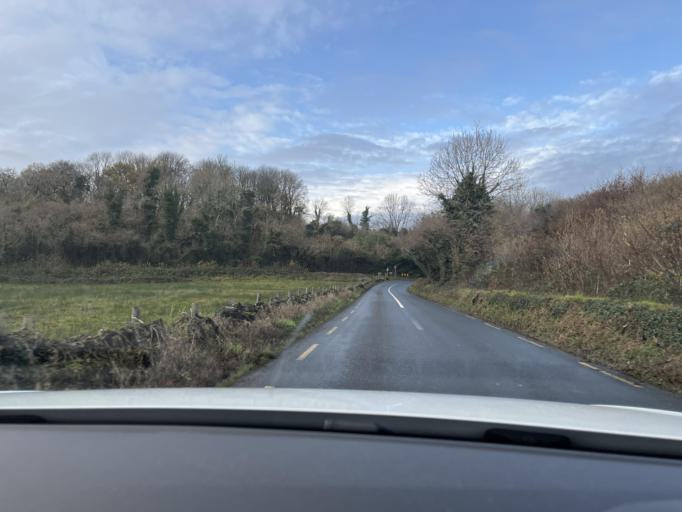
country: IE
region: Connaught
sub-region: Sligo
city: Sligo
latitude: 54.2655
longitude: -8.3651
